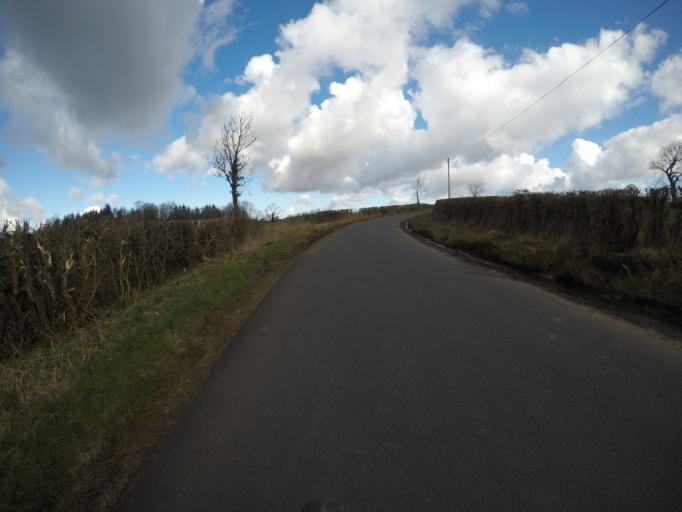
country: GB
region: Scotland
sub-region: North Ayrshire
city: Dalry
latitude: 55.6934
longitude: -4.6747
